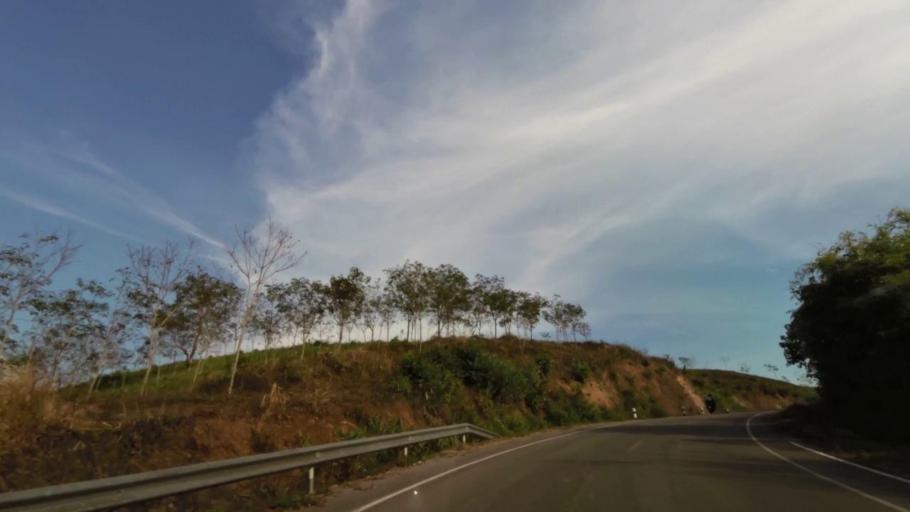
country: TH
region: Chiang Rai
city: Khun Tan
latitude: 19.8644
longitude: 100.3659
